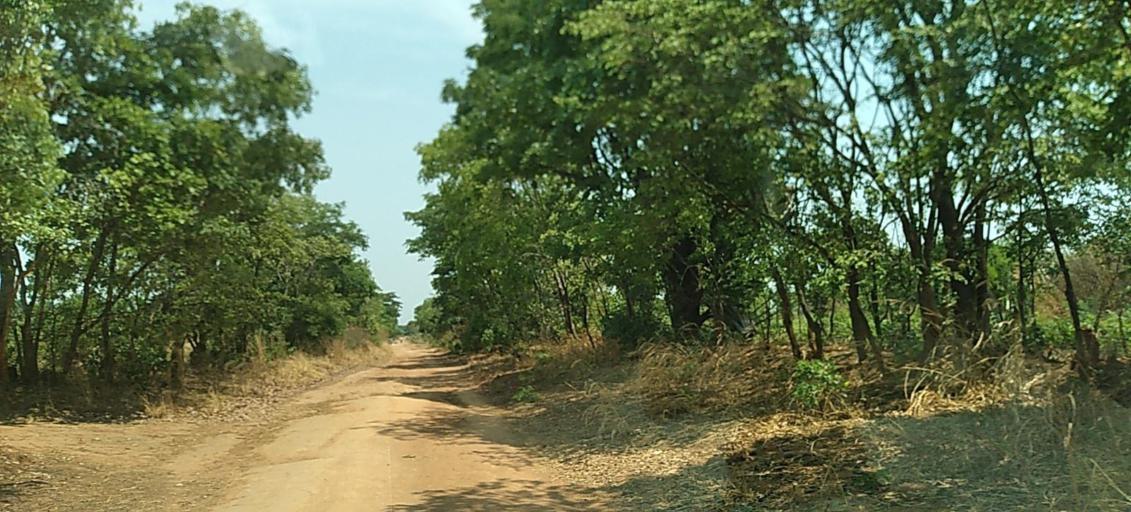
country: ZM
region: Copperbelt
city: Ndola
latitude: -13.0667
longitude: 28.7414
